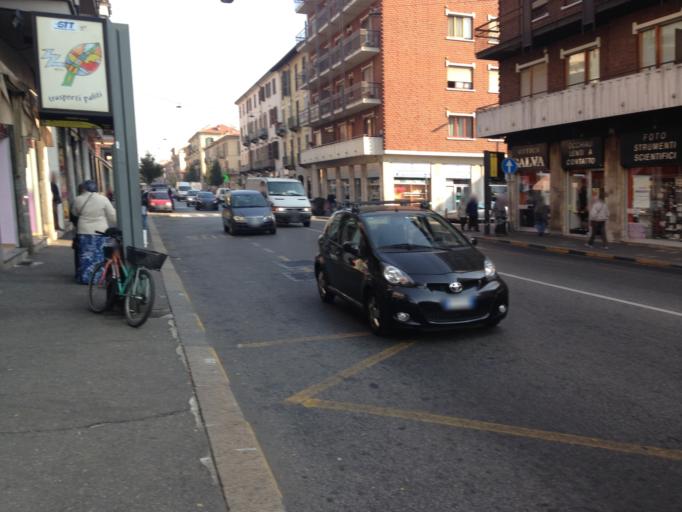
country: IT
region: Piedmont
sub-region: Provincia di Torino
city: Turin
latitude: 45.0900
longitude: 7.6888
